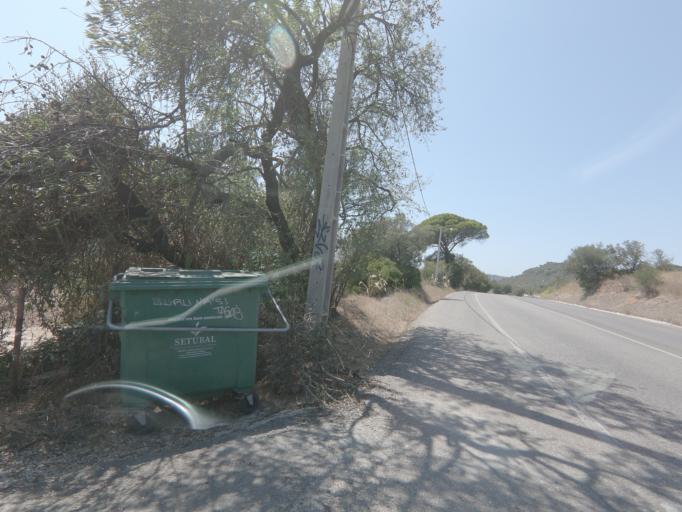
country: PT
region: Setubal
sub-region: Palmela
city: Quinta do Anjo
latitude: 38.5251
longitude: -8.9388
